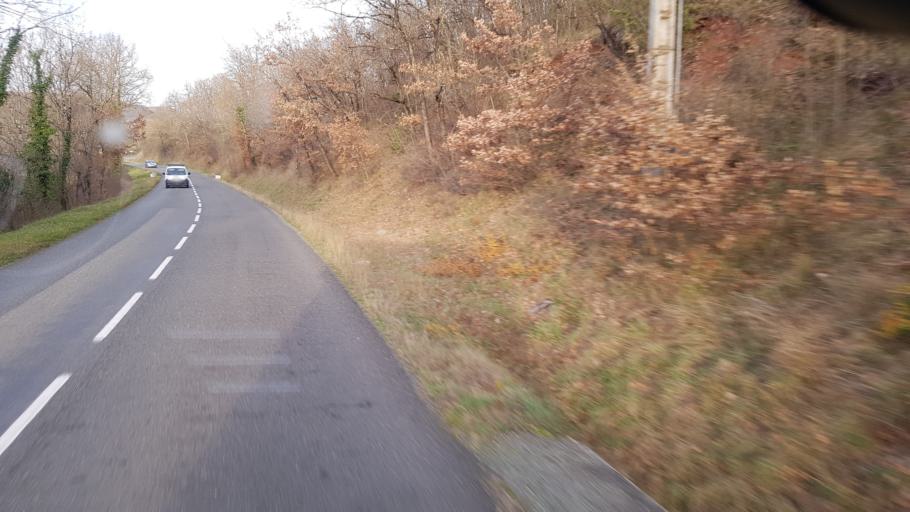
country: FR
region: Midi-Pyrenees
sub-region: Departement du Tarn-et-Garonne
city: Monclar-de-Quercy
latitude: 43.9785
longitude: 1.7243
